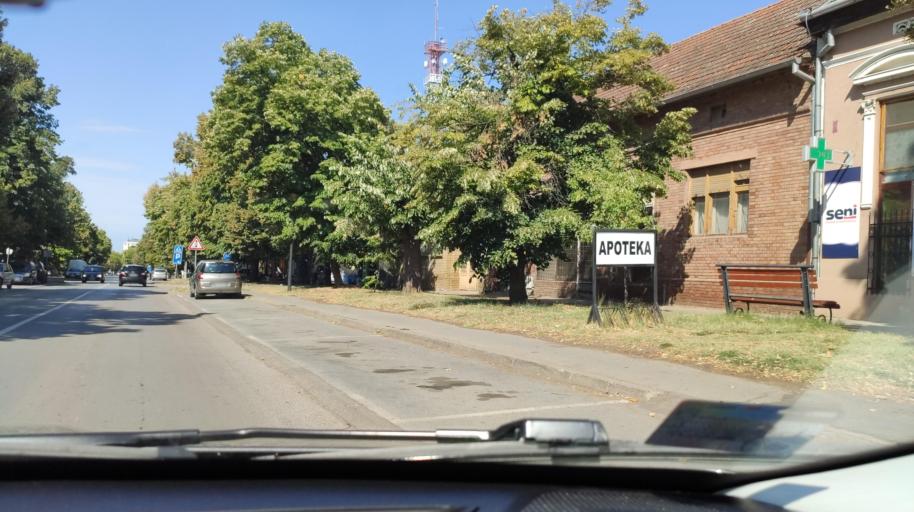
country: RS
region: Autonomna Pokrajina Vojvodina
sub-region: Severnobacki Okrug
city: Backa Topola
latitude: 45.8145
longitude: 19.6398
